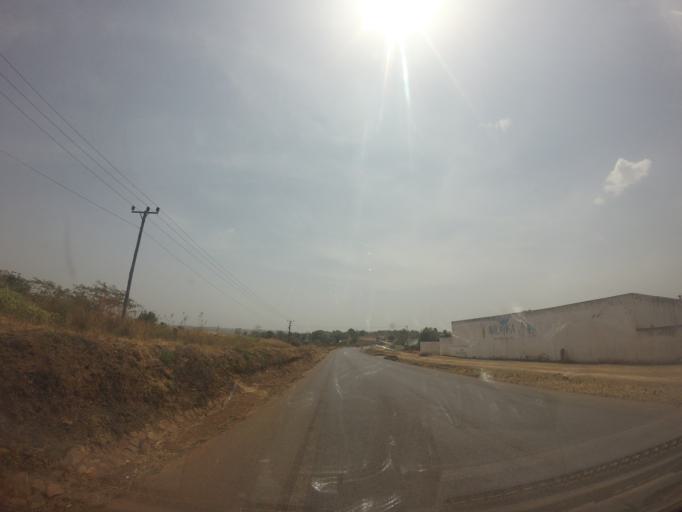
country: UG
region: Northern Region
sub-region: Arua District
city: Arua
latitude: 2.9552
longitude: 30.9288
